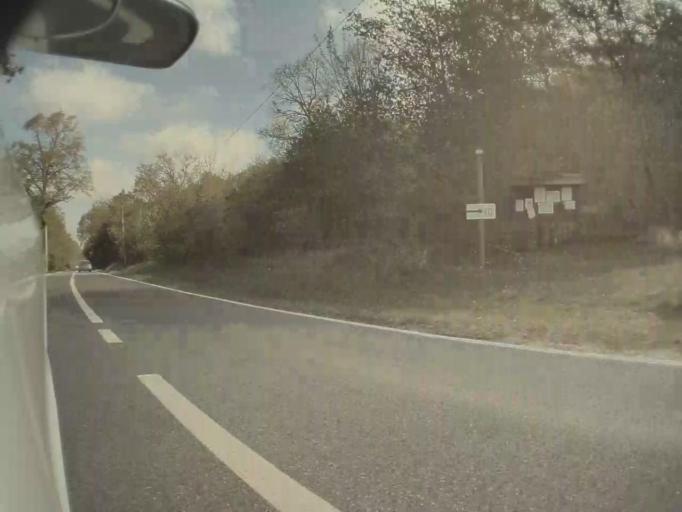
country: BE
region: Wallonia
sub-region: Province du Luxembourg
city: Tellin
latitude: 50.1001
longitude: 5.2310
